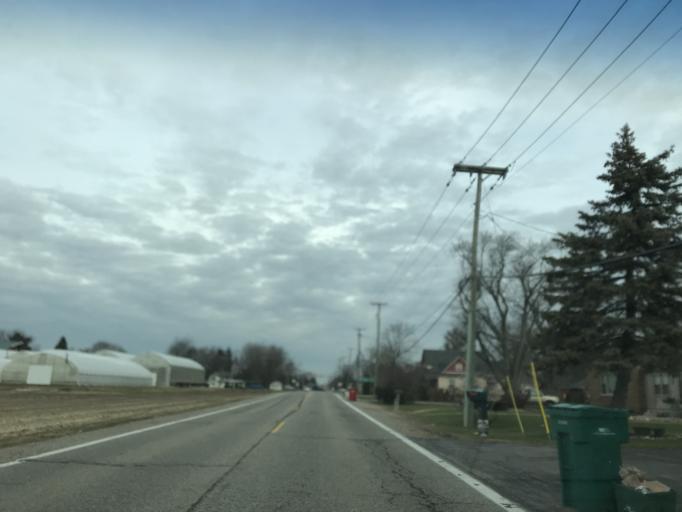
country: US
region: Michigan
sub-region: Macomb County
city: Shelby
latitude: 42.6986
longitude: -82.9589
